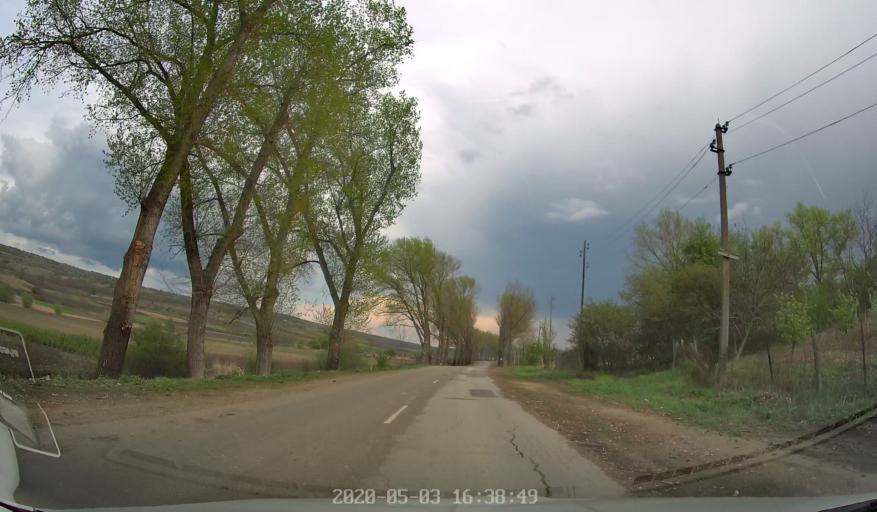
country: MD
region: Calarasi
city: Calarasi
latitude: 47.1874
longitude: 28.3649
